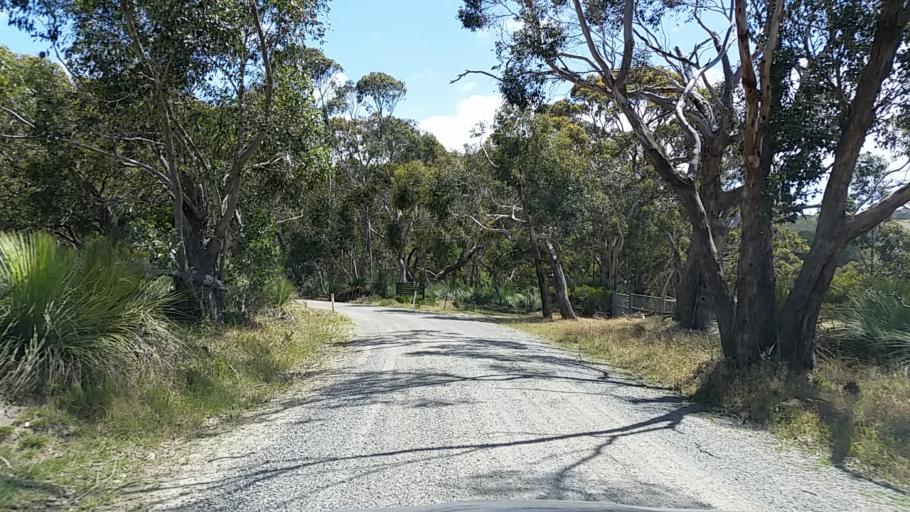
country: AU
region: South Australia
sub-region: Alexandrina
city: Mount Compass
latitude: -35.4374
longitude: 138.5845
